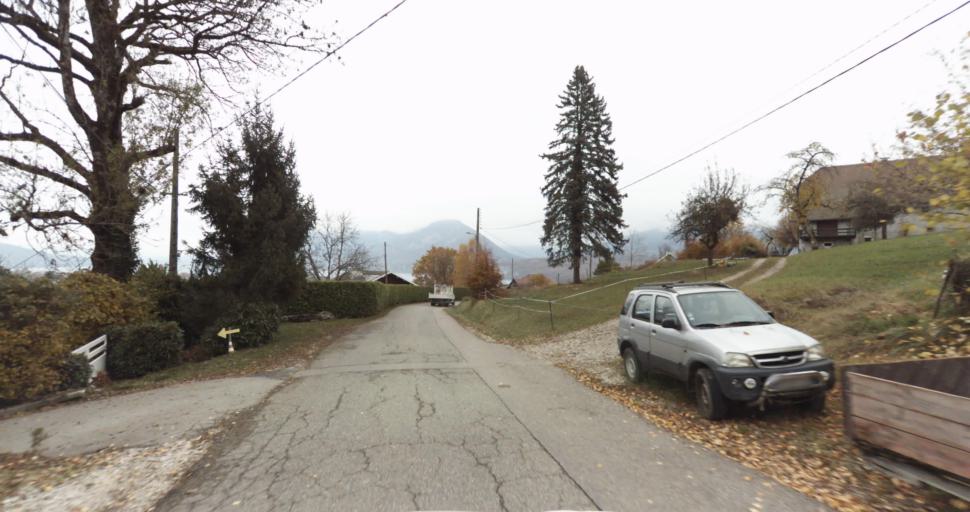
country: FR
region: Rhone-Alpes
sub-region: Departement de la Haute-Savoie
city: Saint-Jorioz
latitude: 45.8227
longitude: 6.1698
